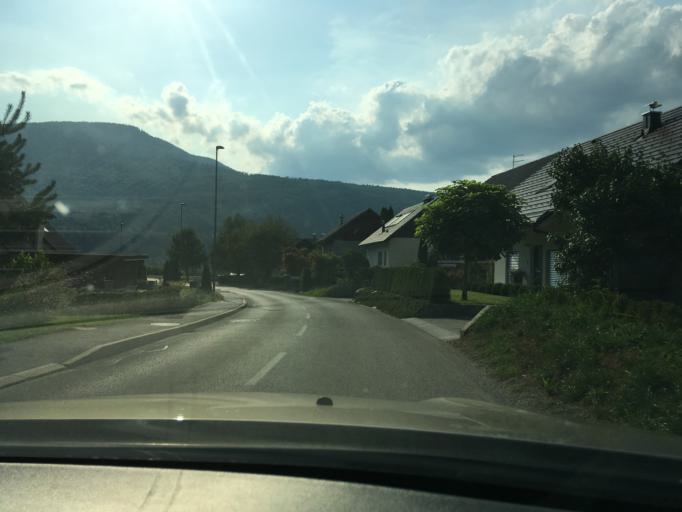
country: SI
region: Dolenjske Toplice
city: Dolenjske Toplice
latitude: 45.7617
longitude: 15.0429
